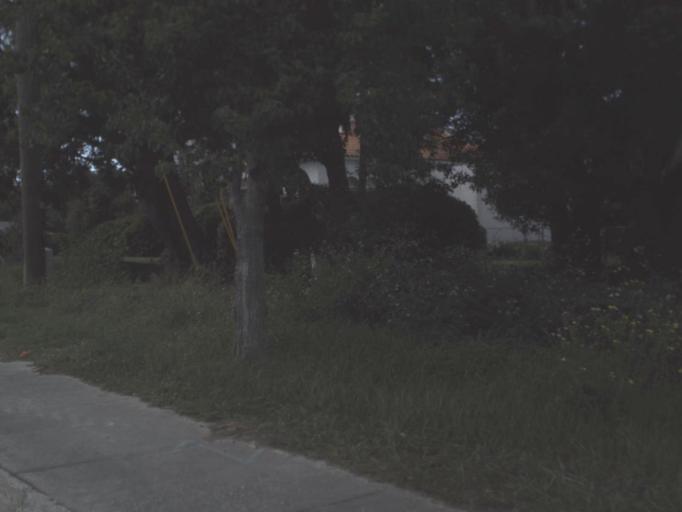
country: US
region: Florida
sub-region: Polk County
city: Haines City
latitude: 28.0890
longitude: -81.6233
